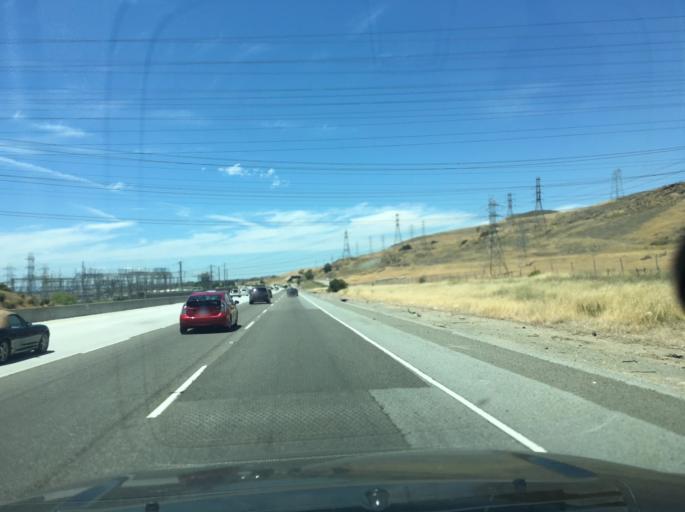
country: US
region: California
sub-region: Santa Clara County
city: Seven Trees
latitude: 37.2231
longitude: -121.7378
